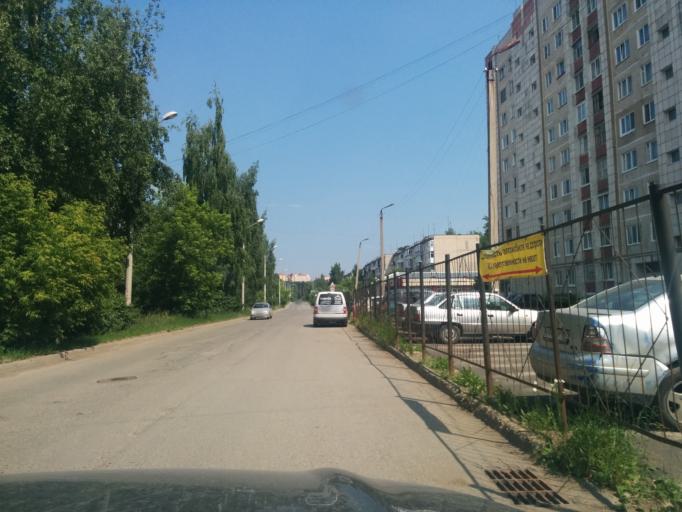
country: RU
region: Perm
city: Kondratovo
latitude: 58.0240
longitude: 56.0026
